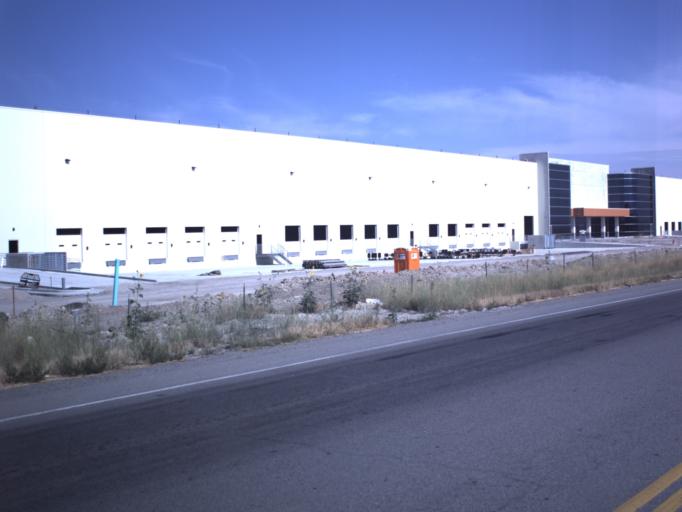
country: US
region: Utah
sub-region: Salt Lake County
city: West Valley City
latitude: 40.7331
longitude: -112.0249
